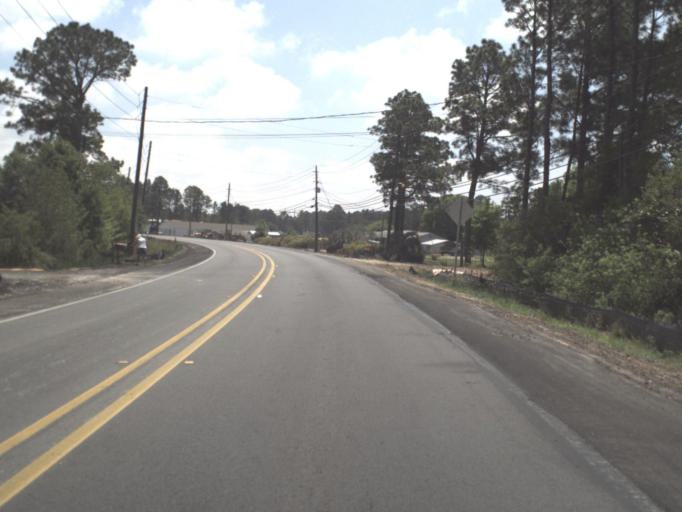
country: US
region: Florida
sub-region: Escambia County
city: Myrtle Grove
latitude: 30.3985
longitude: -87.3176
